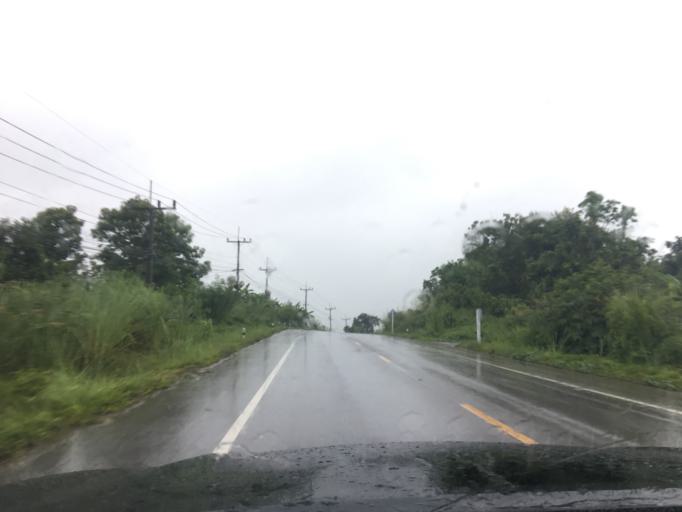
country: TH
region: Chiang Rai
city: Chiang Saen
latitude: 20.2644
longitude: 100.1898
